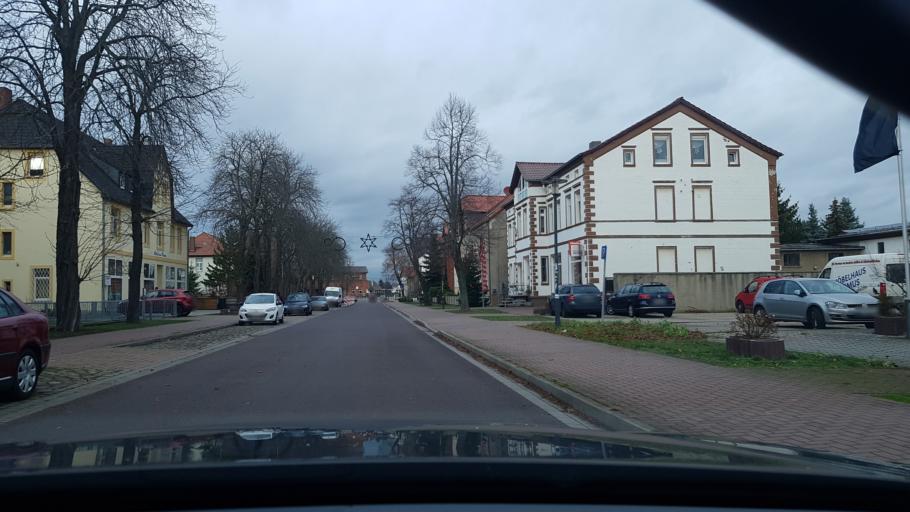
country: DE
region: Saxony-Anhalt
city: Oebisfelde
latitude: 52.4370
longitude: 10.9864
